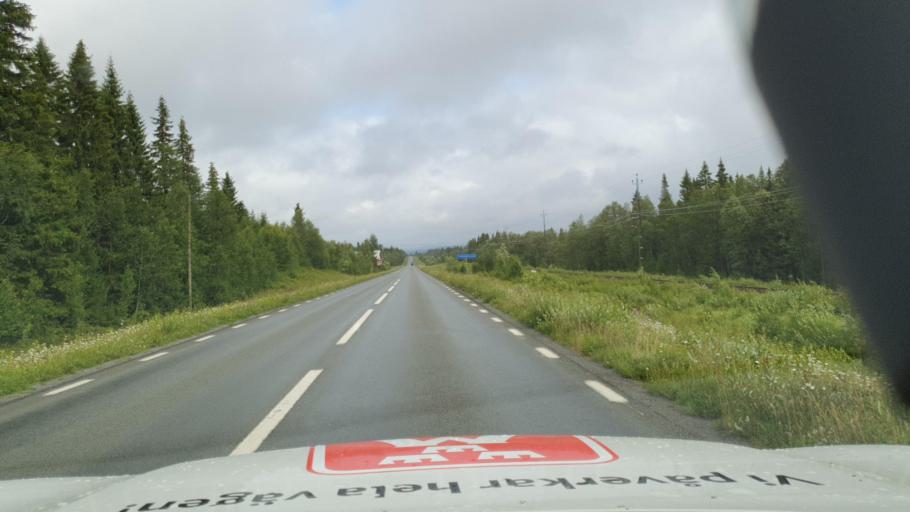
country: SE
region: Jaemtland
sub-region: Are Kommun
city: Are
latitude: 63.3074
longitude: 12.4340
